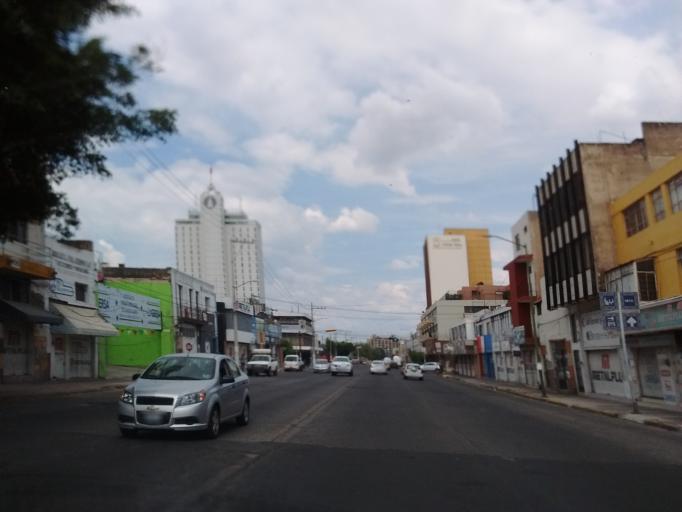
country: MX
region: Jalisco
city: Guadalajara
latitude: 20.6649
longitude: -103.3529
